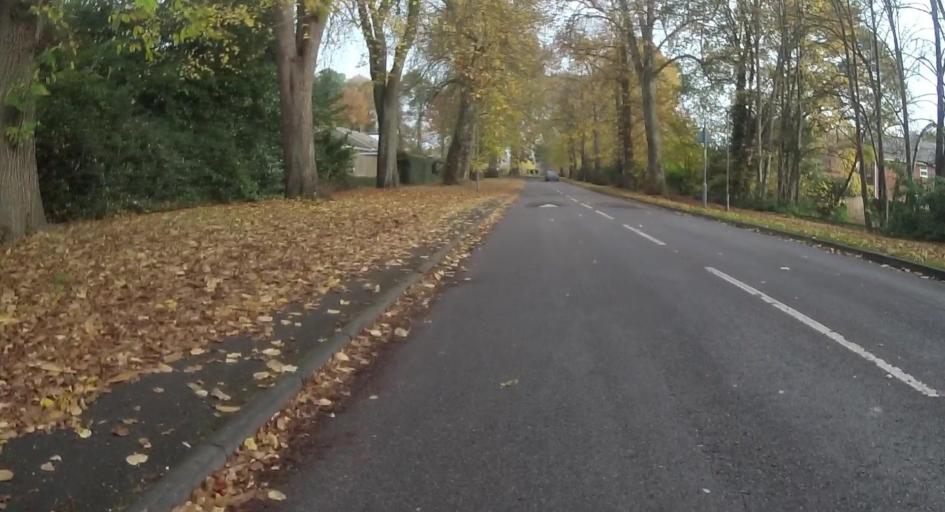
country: GB
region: England
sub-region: Bracknell Forest
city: Crowthorne
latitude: 51.3658
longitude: -0.7894
